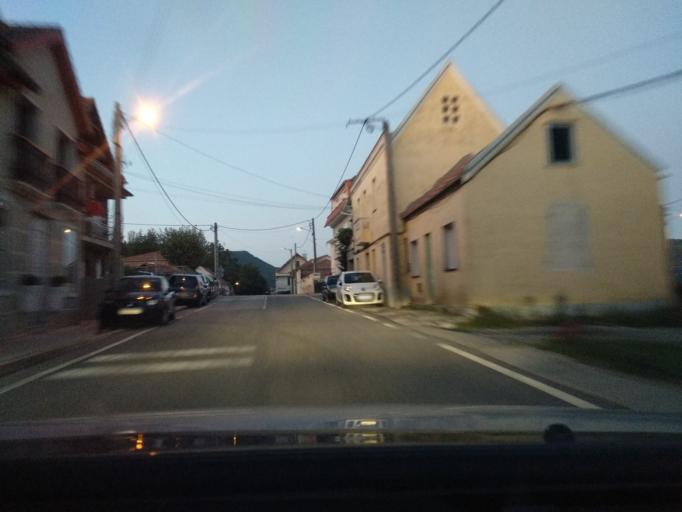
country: ES
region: Galicia
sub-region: Provincia de Pontevedra
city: Moana
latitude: 42.2822
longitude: -8.7440
